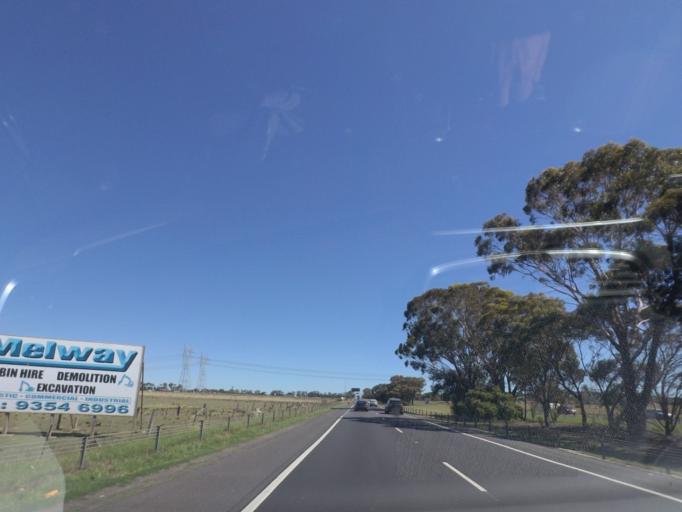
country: AU
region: Victoria
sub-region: Hume
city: Craigieburn
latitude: -37.5519
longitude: 144.9438
